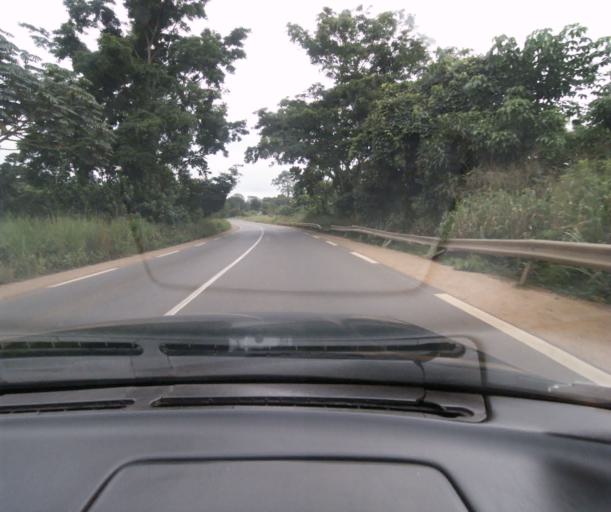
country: CM
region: Centre
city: Obala
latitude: 4.2037
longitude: 11.4506
